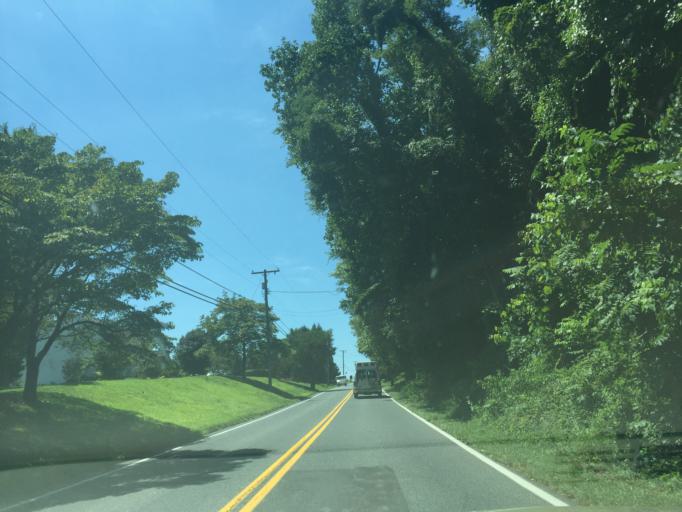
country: US
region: Maryland
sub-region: Harford County
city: Bel Air North
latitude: 39.6015
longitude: -76.3885
